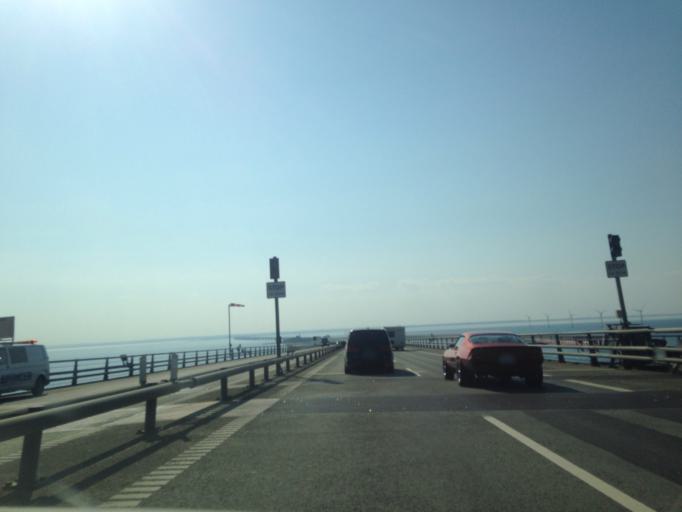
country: DK
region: Zealand
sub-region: Slagelse Kommune
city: Korsor
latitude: 55.3392
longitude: 11.0153
